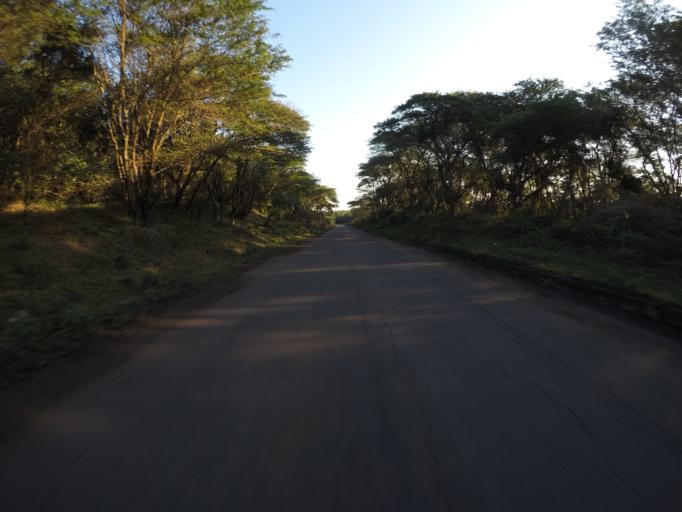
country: ZA
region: KwaZulu-Natal
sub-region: uThungulu District Municipality
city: KwaMbonambi
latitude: -28.6977
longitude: 32.2076
